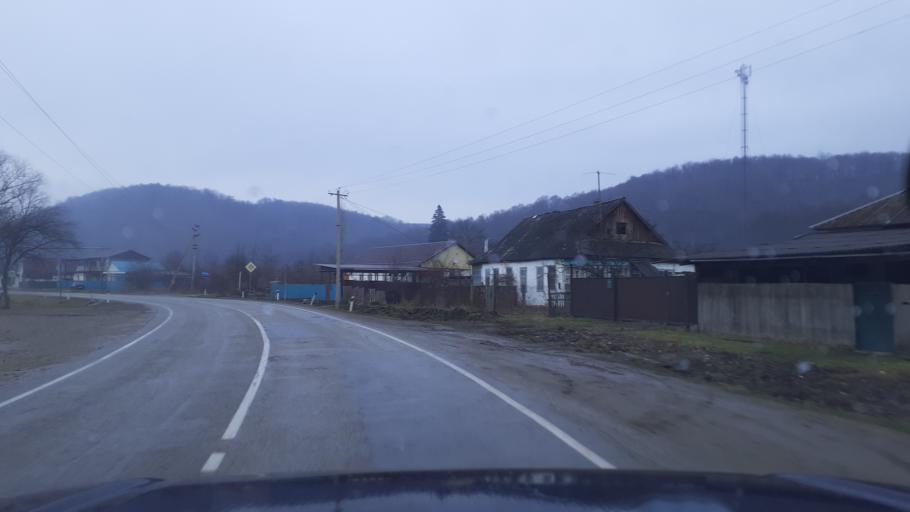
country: RU
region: Krasnodarskiy
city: Neftegorsk
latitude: 44.2988
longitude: 39.8350
